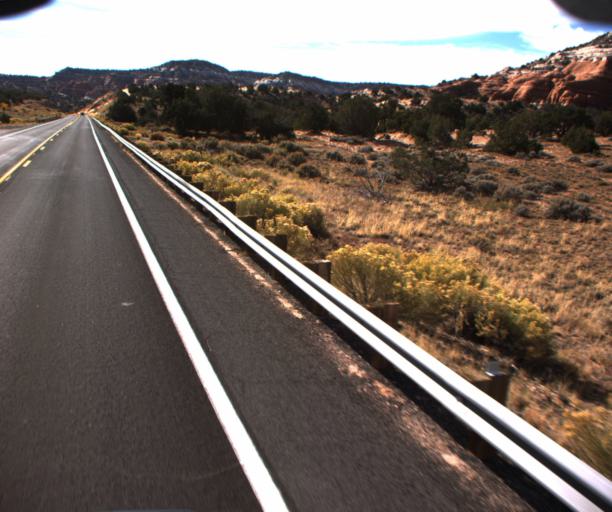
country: US
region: Arizona
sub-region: Coconino County
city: Kaibito
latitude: 36.6095
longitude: -110.9215
